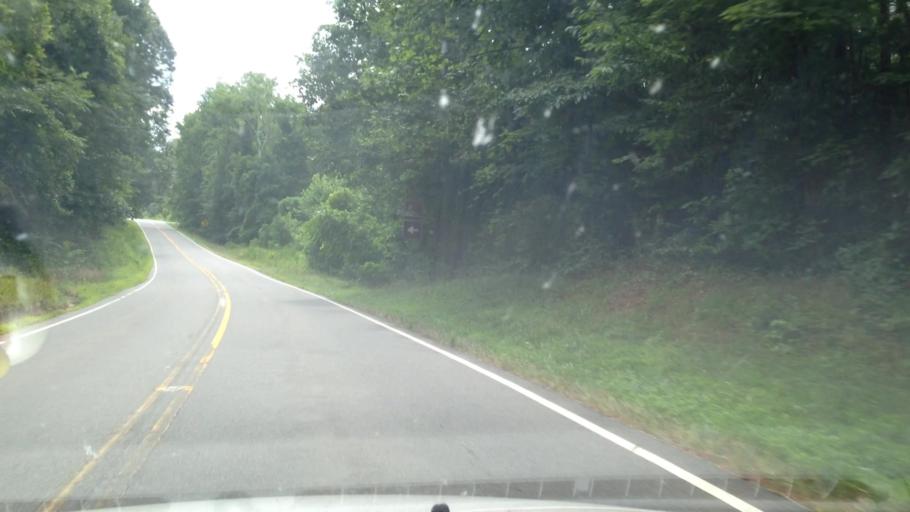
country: US
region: North Carolina
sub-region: Rockingham County
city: Wentworth
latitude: 36.3967
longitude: -79.7949
